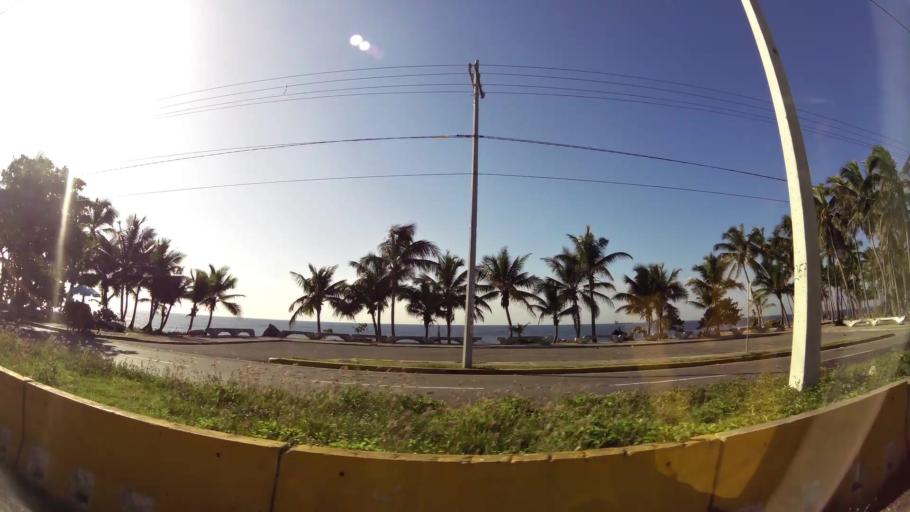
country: DO
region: Nacional
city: Ciudad Nueva
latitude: 18.4660
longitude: -69.8745
